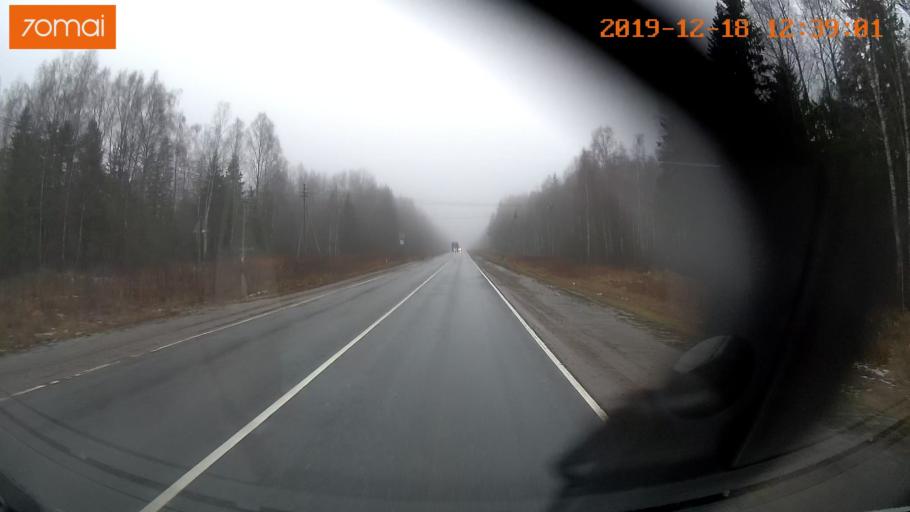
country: RU
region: Moskovskaya
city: Vysokovsk
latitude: 56.1593
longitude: 36.6086
